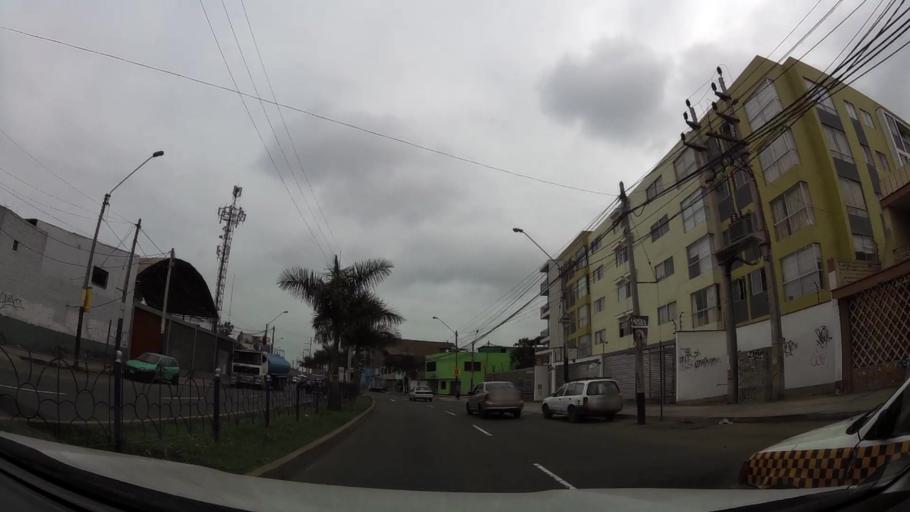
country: PE
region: Lima
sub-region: Lima
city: Surco
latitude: -12.1750
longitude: -77.0003
